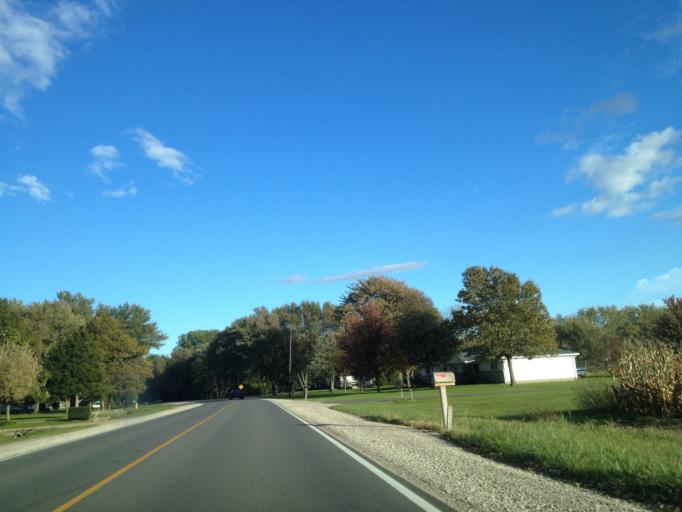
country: US
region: Michigan
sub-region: Wayne County
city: Grosse Pointe Farms
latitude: 42.2969
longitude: -82.6670
